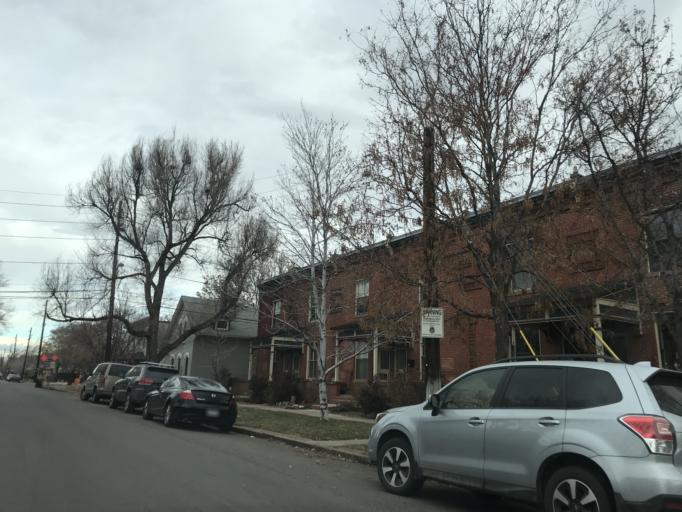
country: US
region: Colorado
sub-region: Denver County
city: Denver
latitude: 39.7609
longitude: -104.9739
